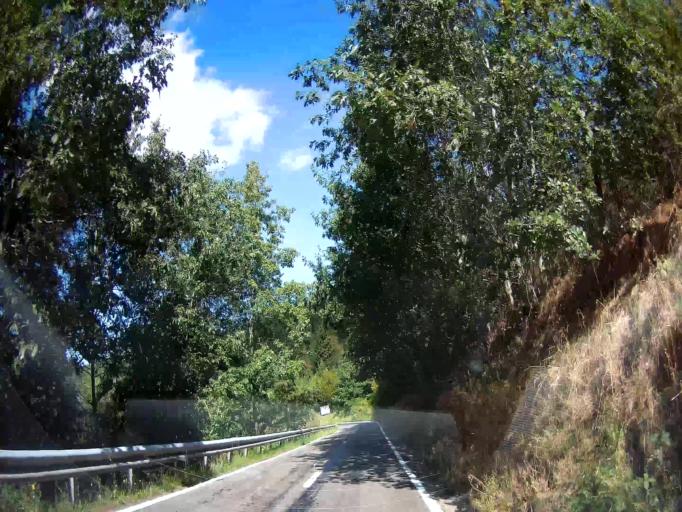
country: BE
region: Wallonia
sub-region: Province du Luxembourg
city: La Roche-en-Ardenne
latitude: 50.1667
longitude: 5.5913
